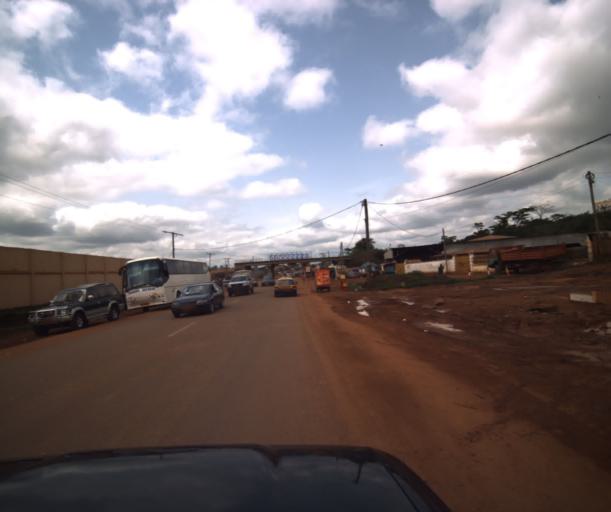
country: CM
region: Centre
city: Yaounde
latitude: 3.8033
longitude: 11.5079
